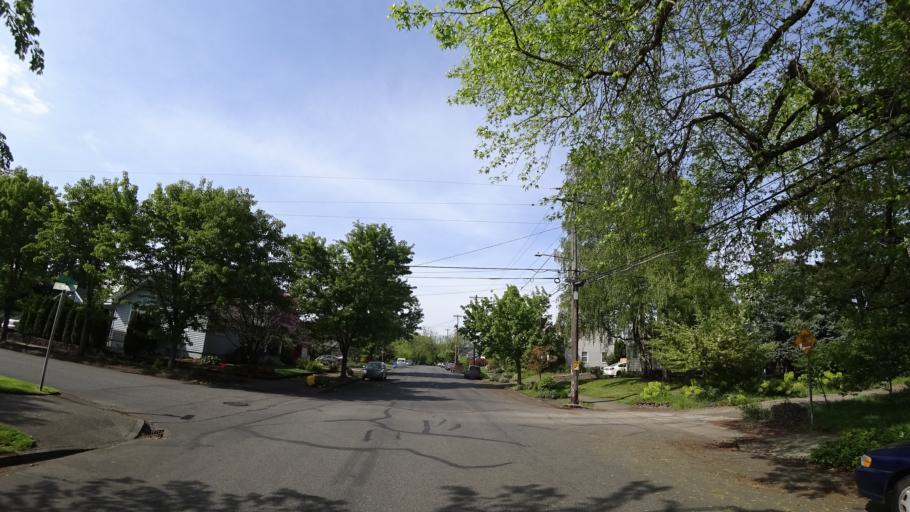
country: US
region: Oregon
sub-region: Clackamas County
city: Milwaukie
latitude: 45.4769
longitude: -122.6196
